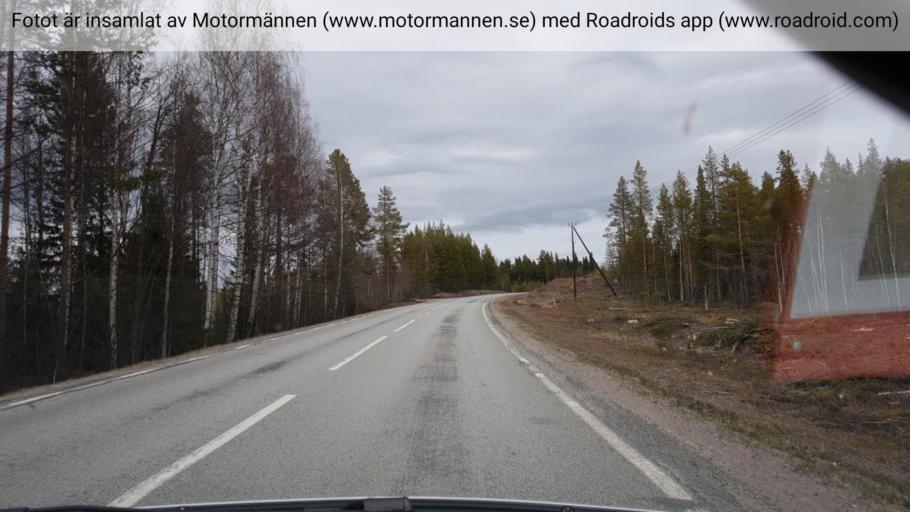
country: SE
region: Vaesterbotten
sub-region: Asele Kommun
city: Asele
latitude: 63.9121
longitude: 17.2254
